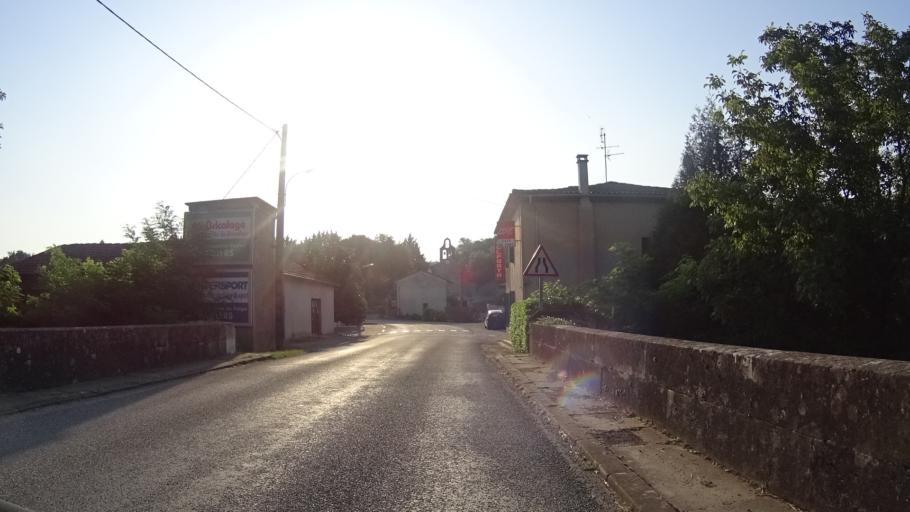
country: FR
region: Midi-Pyrenees
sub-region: Departement de l'Ariege
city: Mirepoix
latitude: 43.0742
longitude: 1.9436
